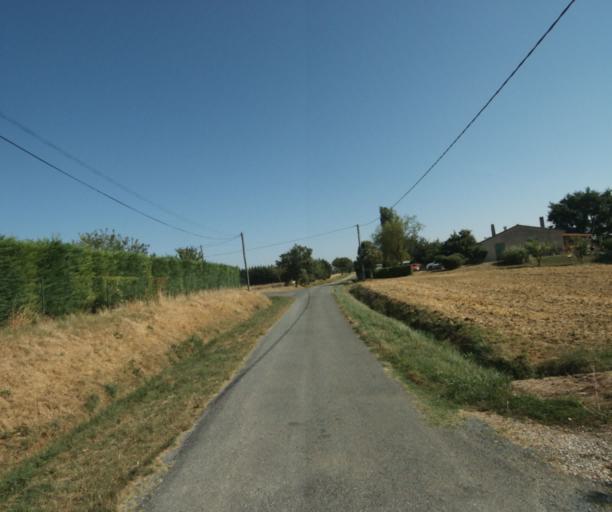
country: FR
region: Midi-Pyrenees
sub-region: Departement de la Haute-Garonne
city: Saint-Felix-Lauragais
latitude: 43.4829
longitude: 1.9173
